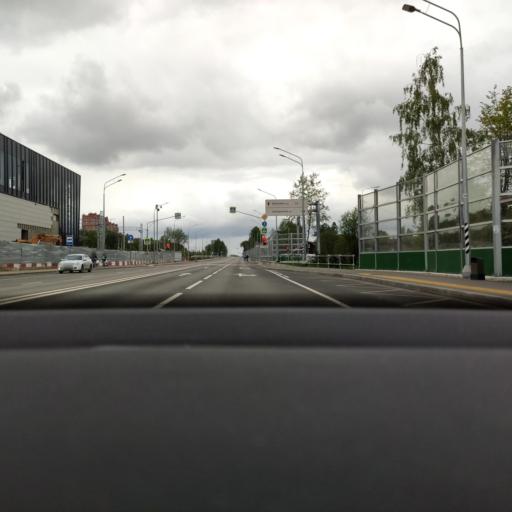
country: RU
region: Moscow
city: Severnyy
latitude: 55.9242
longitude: 37.5287
